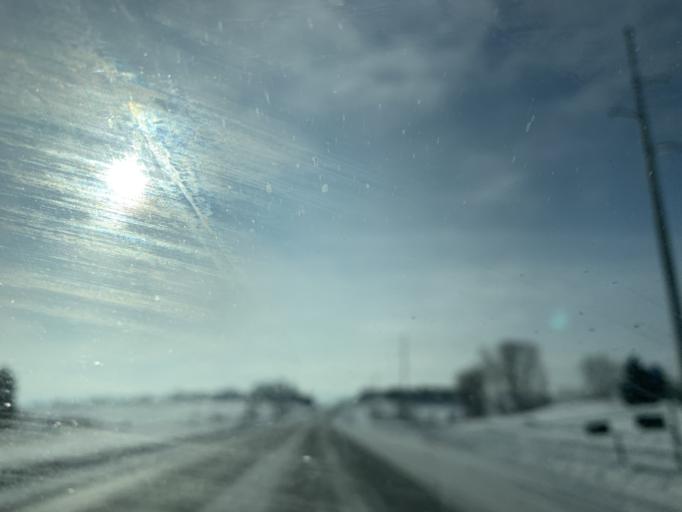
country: US
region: Minnesota
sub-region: Dakota County
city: Lakeville
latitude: 44.6765
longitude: -93.2172
